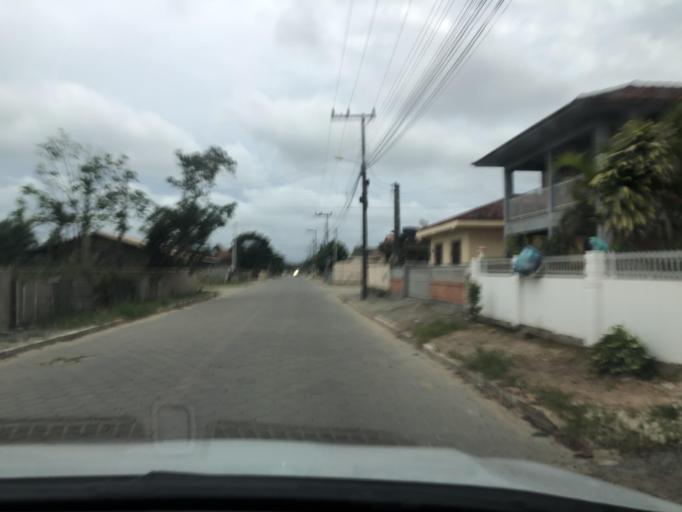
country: BR
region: Santa Catarina
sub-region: Sao Francisco Do Sul
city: Sao Francisco do Sul
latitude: -26.2275
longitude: -48.5252
